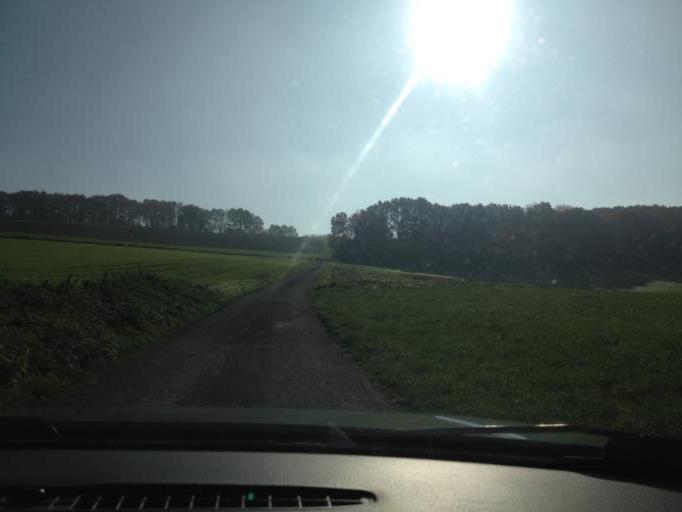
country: DE
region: Saarland
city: Sankt Wendel
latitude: 49.4939
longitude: 7.1886
